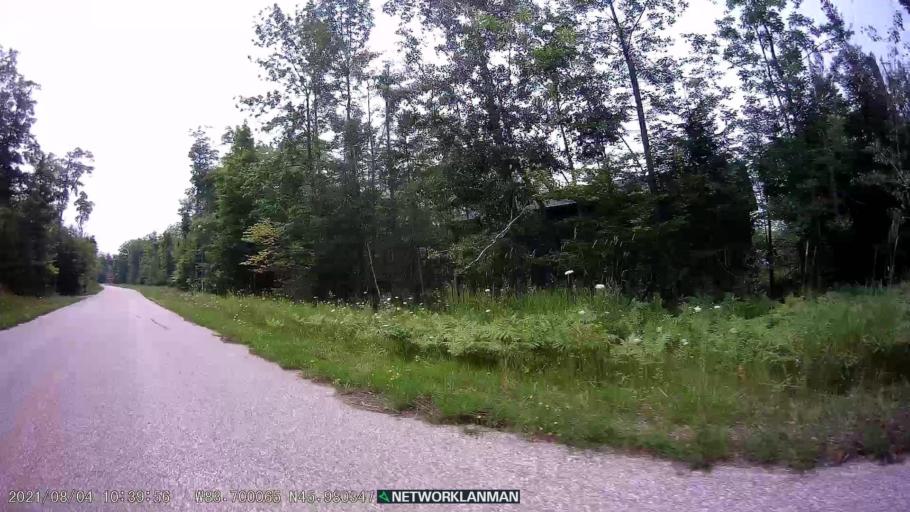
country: CA
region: Ontario
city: Thessalon
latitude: 45.9791
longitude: -83.7002
